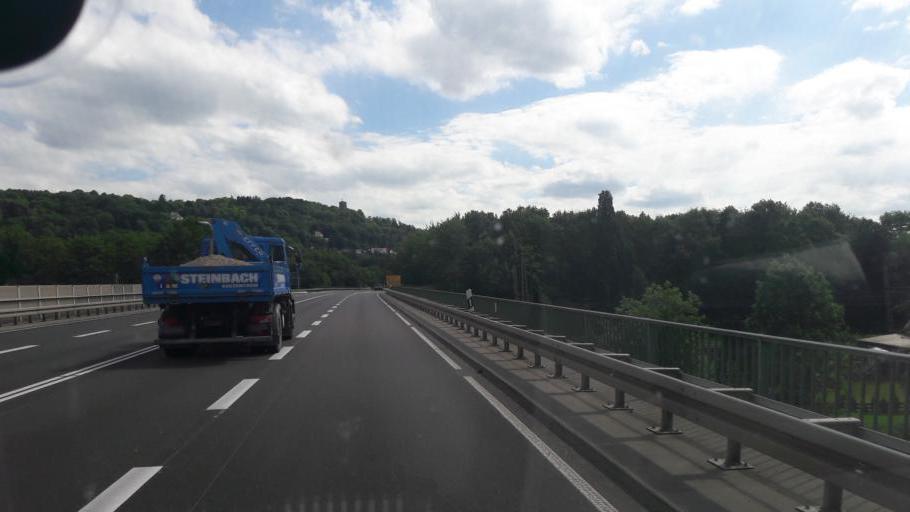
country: DE
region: Baden-Wuerttemberg
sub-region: Karlsruhe Region
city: Weingarten
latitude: 49.0086
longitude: 8.4878
